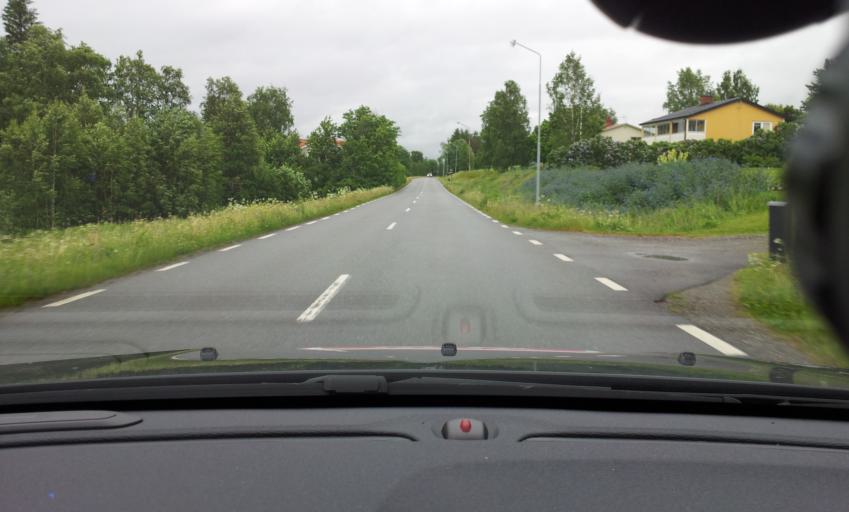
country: SE
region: Jaemtland
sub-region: Stroemsunds Kommun
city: Stroemsund
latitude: 63.5781
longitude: 15.3682
